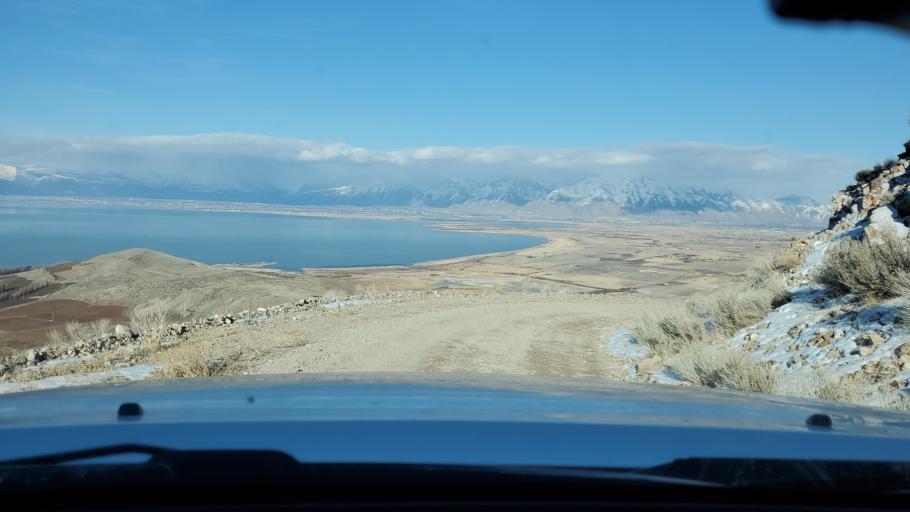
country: US
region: Utah
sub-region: Utah County
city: West Mountain
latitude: 40.1170
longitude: -111.8232
